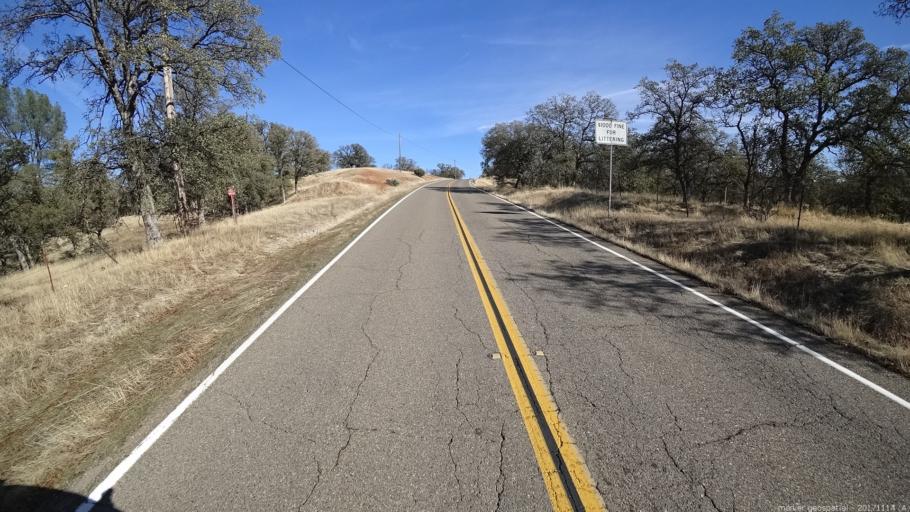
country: US
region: California
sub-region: Shasta County
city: Anderson
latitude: 40.4076
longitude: -122.3518
